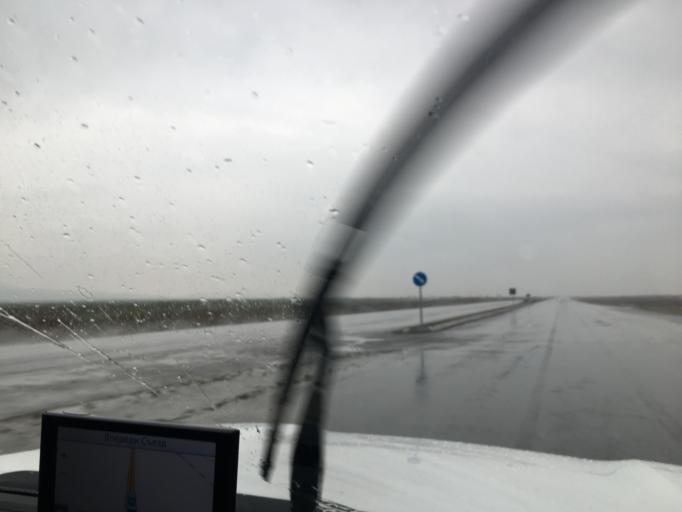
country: TM
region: Ahal
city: Annau
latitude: 37.8055
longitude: 58.7914
